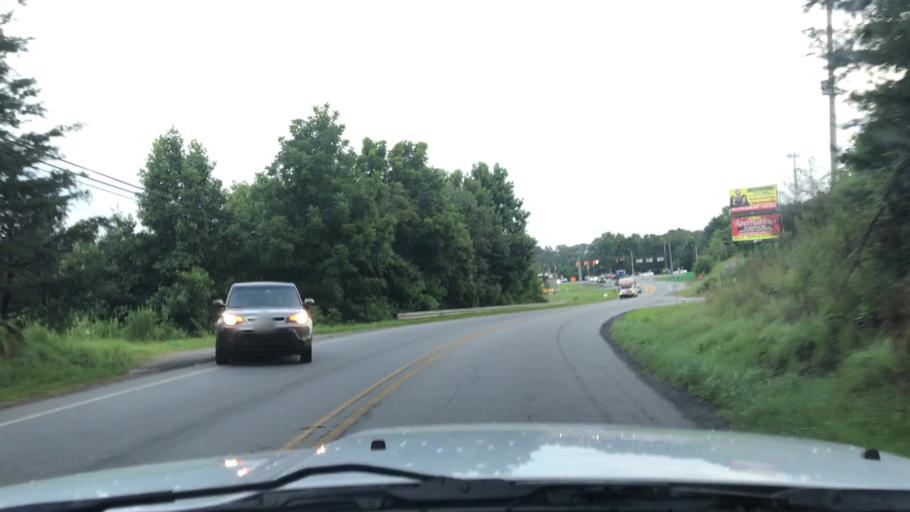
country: US
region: Georgia
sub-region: Fannin County
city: Blue Ridge
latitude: 34.8958
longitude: -84.2624
